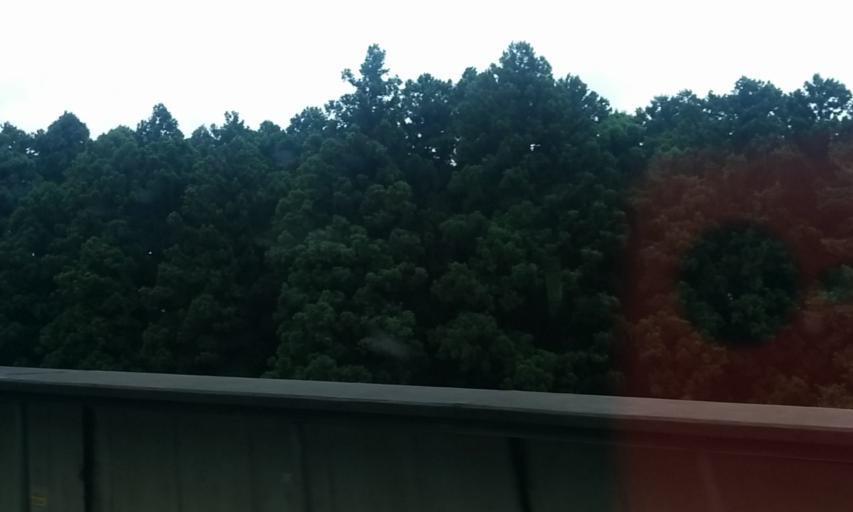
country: JP
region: Tochigi
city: Kuroiso
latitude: 36.9416
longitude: 140.0313
